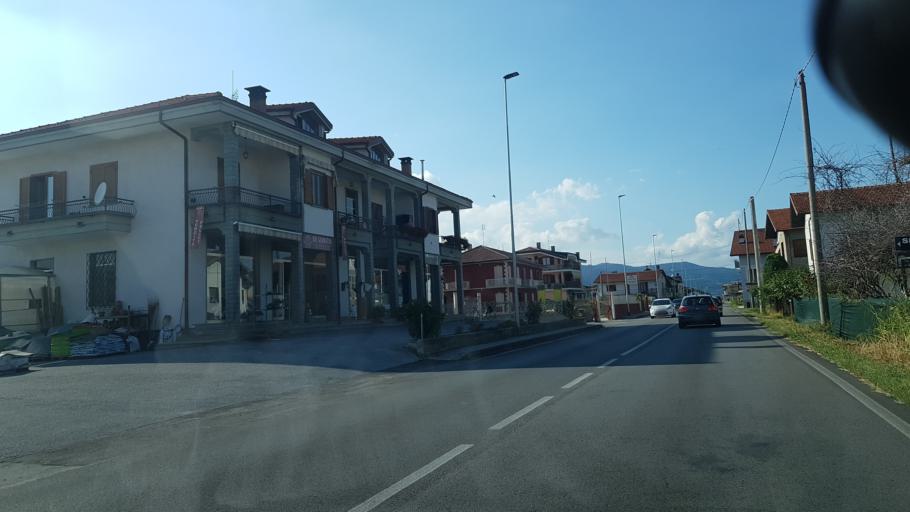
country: IT
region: Piedmont
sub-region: Provincia di Cuneo
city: Roata Rossi
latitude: 44.4772
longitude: 7.5073
